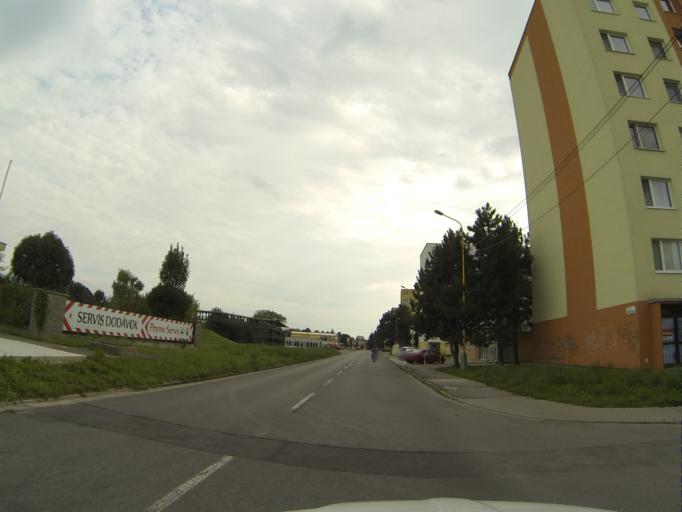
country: SK
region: Nitriansky
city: Prievidza
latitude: 48.7799
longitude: 18.6200
